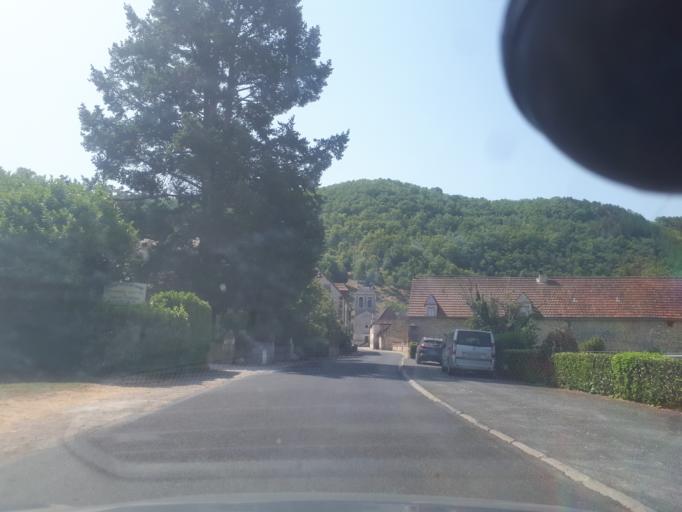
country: FR
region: Midi-Pyrenees
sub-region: Departement du Lot
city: Souillac
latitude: 44.8673
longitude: 1.4410
